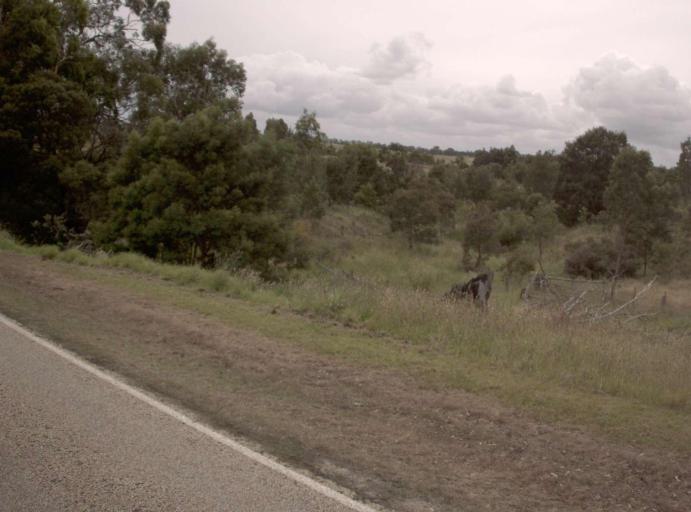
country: AU
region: Victoria
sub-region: Wellington
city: Sale
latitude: -37.9427
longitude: 147.0919
